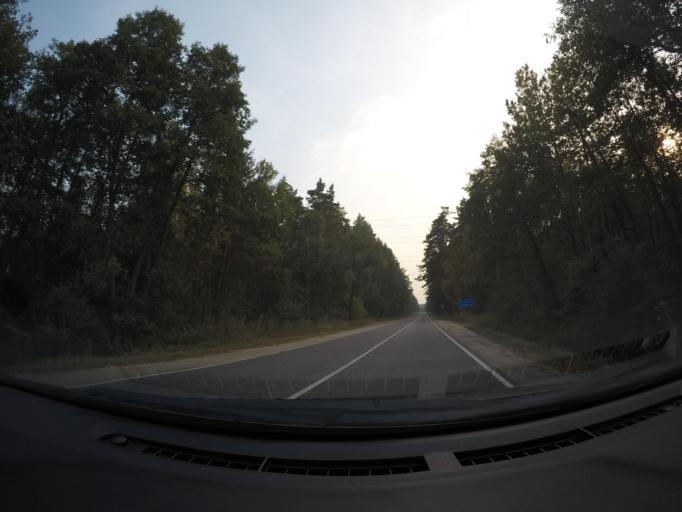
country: RU
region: Moskovskaya
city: Imeni Tsyurupy
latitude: 55.5156
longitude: 38.7240
